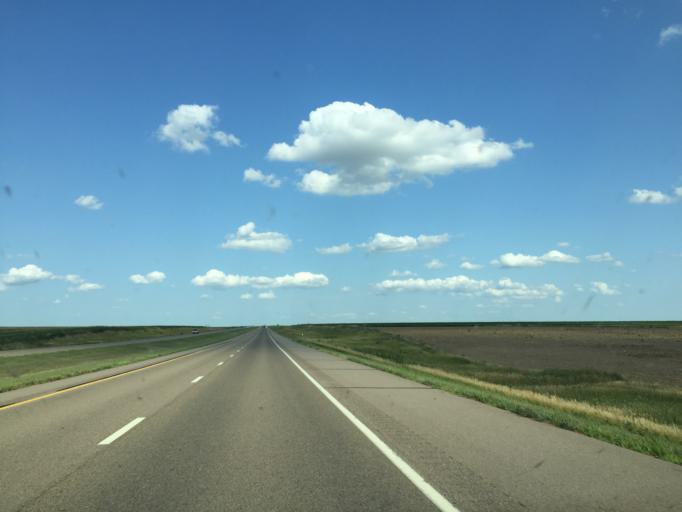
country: US
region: Kansas
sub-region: Trego County
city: WaKeeney
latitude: 39.0231
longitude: -100.0496
